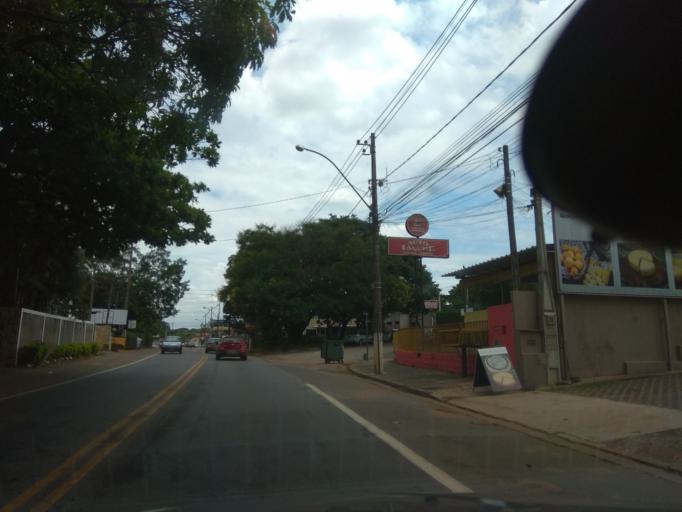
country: BR
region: Sao Paulo
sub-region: Campinas
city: Campinas
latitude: -22.8172
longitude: -47.0812
